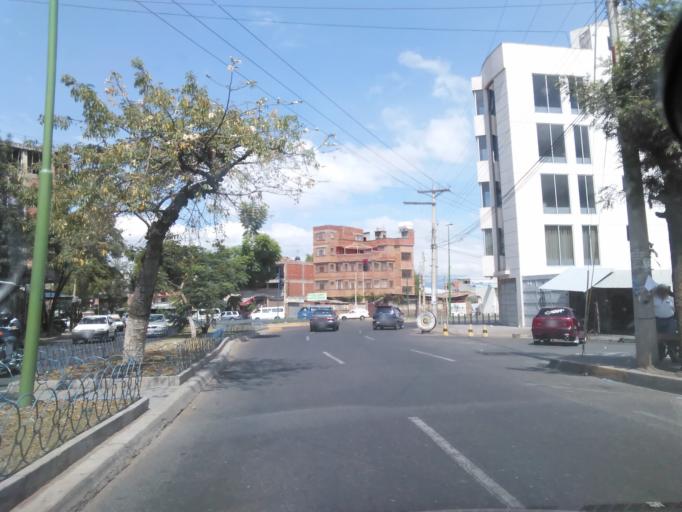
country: BO
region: Cochabamba
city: Cochabamba
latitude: -17.4000
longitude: -66.1621
